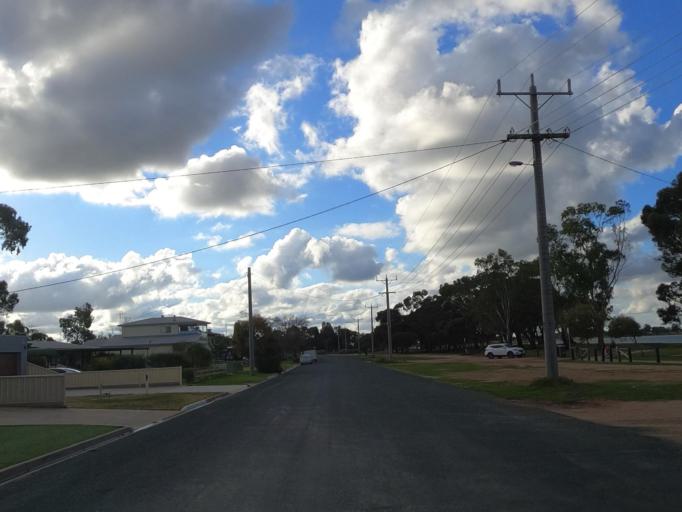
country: AU
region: Victoria
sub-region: Swan Hill
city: Swan Hill
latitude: -35.4499
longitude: 143.6276
